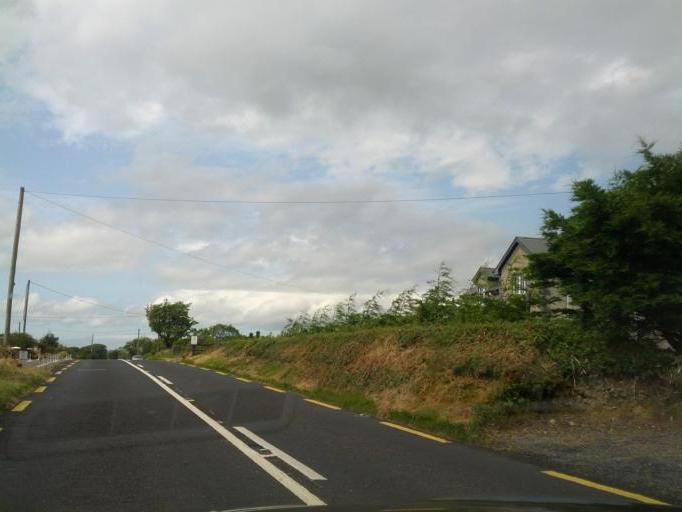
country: IE
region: Munster
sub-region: An Clar
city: Kilrush
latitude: 52.6472
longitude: -9.5005
